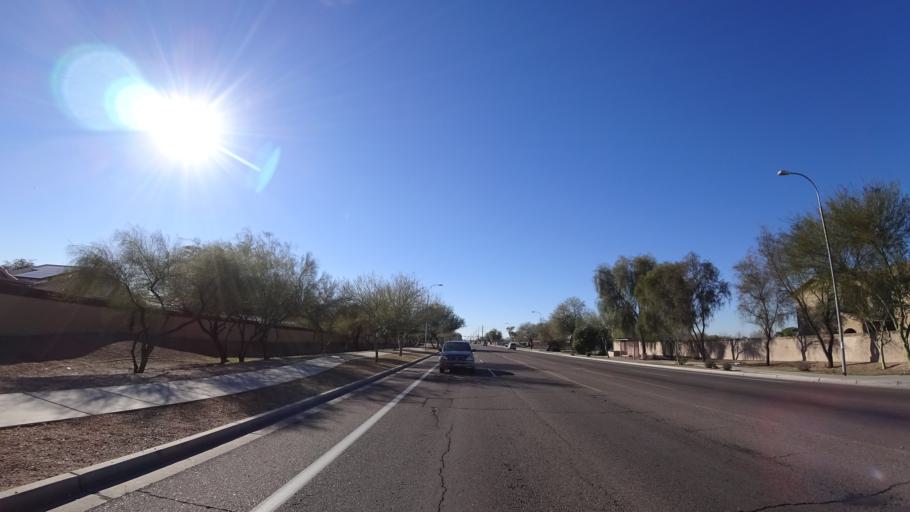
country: US
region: Arizona
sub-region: Maricopa County
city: Phoenix
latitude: 33.3922
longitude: -112.0868
